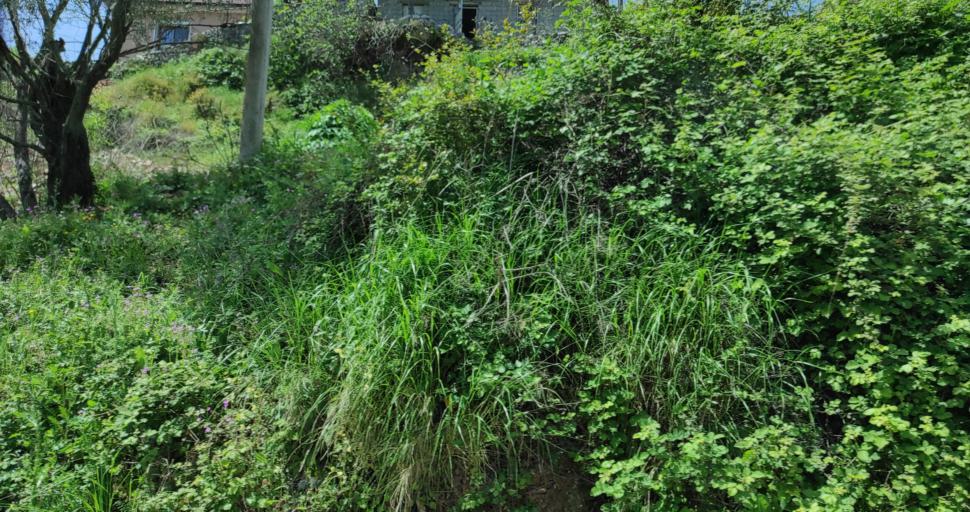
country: AL
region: Shkoder
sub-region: Rrethi i Shkodres
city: Guri i Zi
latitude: 42.1228
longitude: 19.5920
